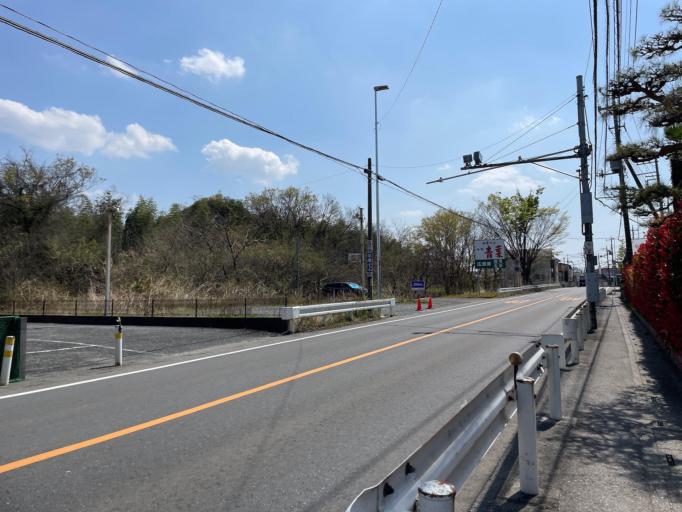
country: JP
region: Saitama
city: Sayama
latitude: 35.8704
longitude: 139.4044
